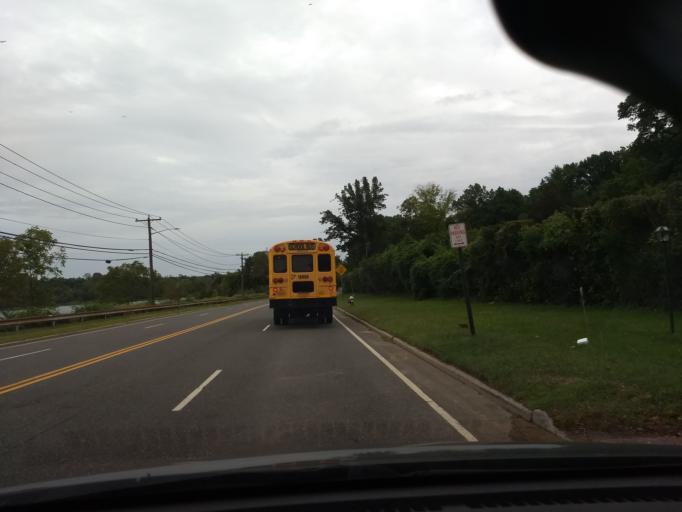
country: US
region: New York
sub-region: Nassau County
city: Great Neck Gardens
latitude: 40.8034
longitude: -73.7159
